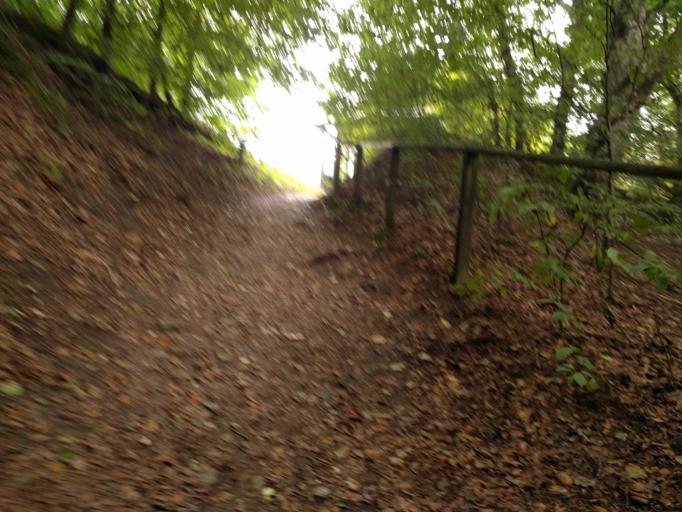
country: DK
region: Central Jutland
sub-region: Viborg Kommune
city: Stoholm
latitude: 56.4437
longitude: 9.1384
